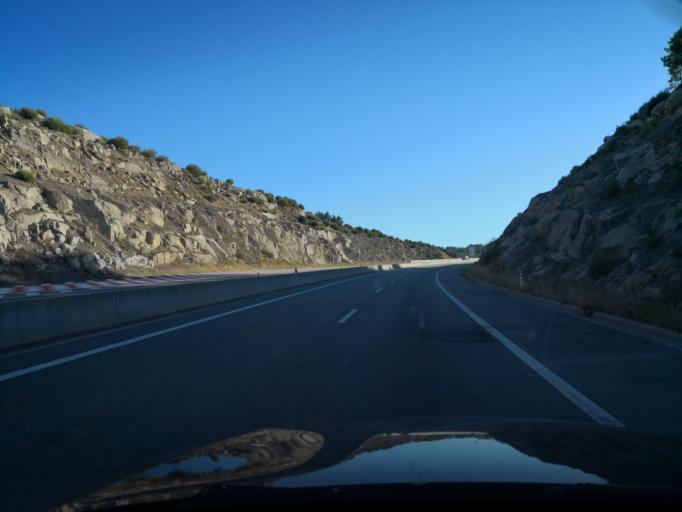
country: PT
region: Vila Real
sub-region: Murca
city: Murca
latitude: 41.3838
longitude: -7.4810
